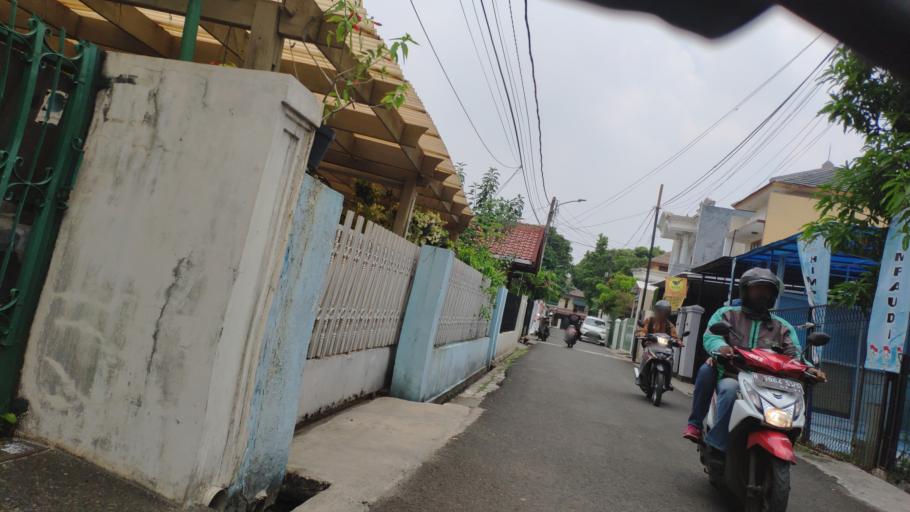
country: ID
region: Jakarta Raya
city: Jakarta
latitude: -6.2700
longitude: 106.7964
